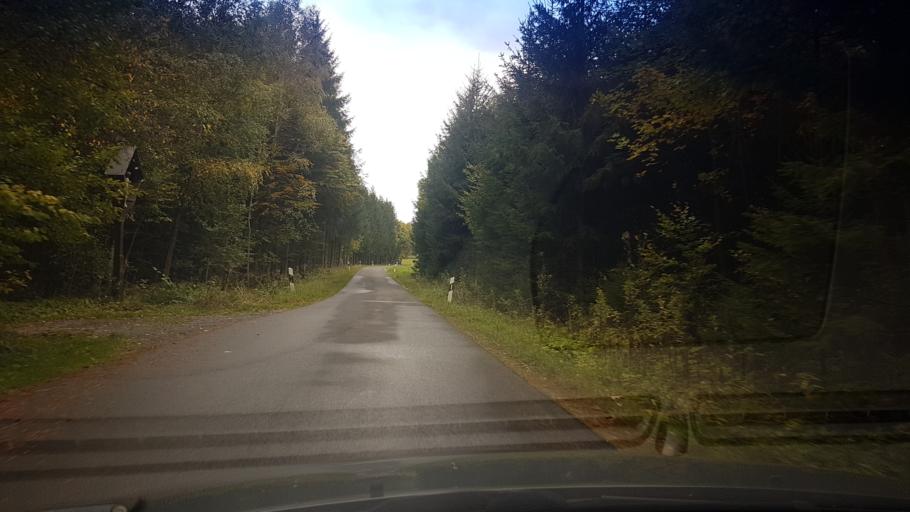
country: DE
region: Bavaria
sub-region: Upper Franconia
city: Stadelhofen
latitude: 50.0028
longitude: 11.2122
